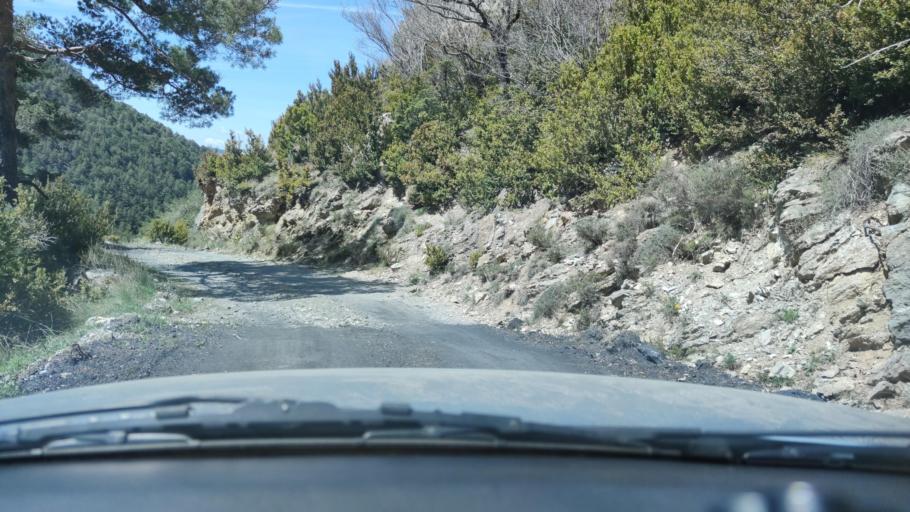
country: ES
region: Catalonia
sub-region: Provincia de Lleida
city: Sort
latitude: 42.3088
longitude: 1.1625
